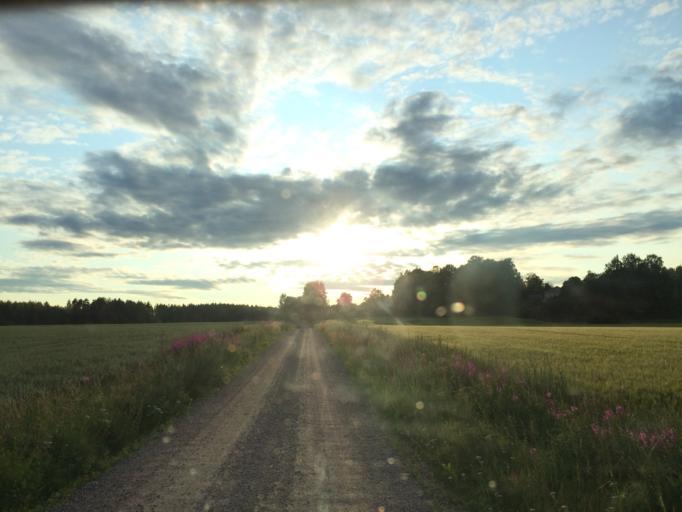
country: FI
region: Haeme
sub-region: Haemeenlinna
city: Janakkala
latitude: 60.8869
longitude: 24.6252
